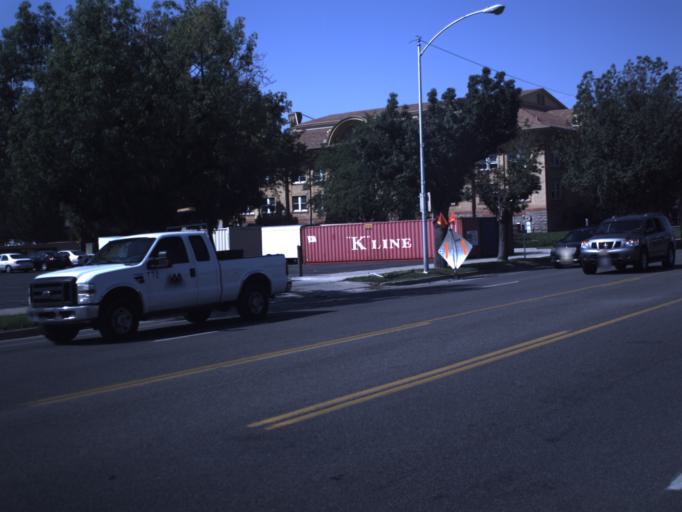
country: US
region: Utah
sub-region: Utah County
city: American Fork
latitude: 40.3768
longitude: -111.7944
